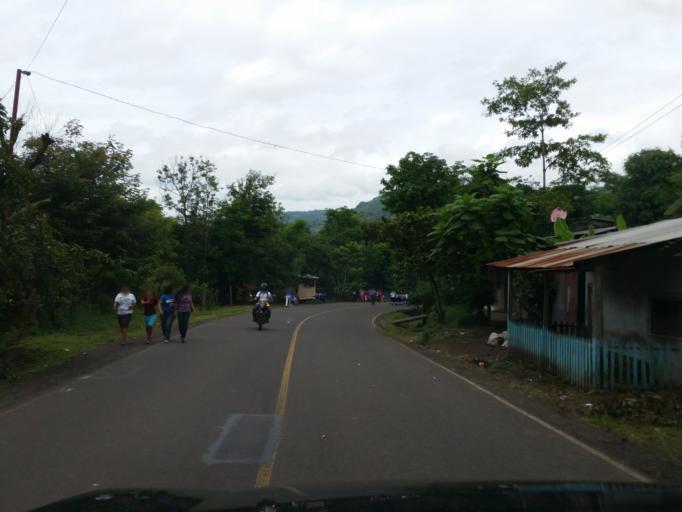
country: NI
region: Matagalpa
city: San Ramon
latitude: 13.0536
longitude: -85.7560
